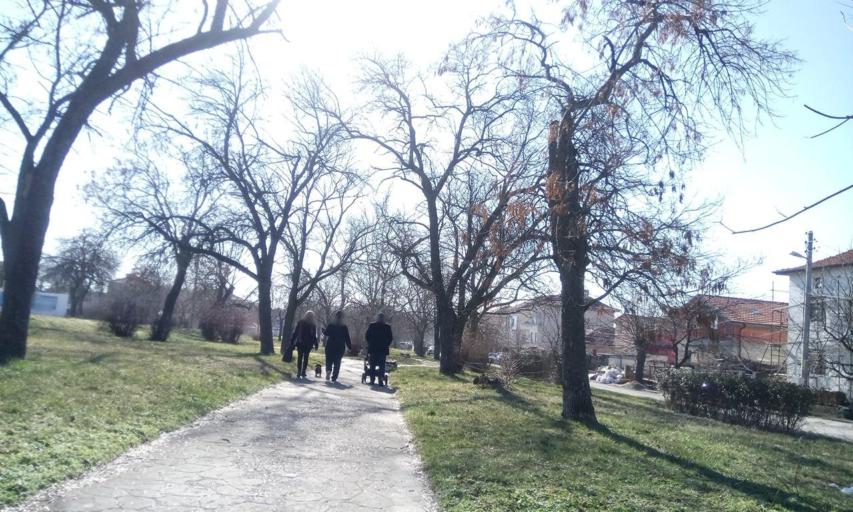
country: BG
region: Plovdiv
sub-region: Obshtina Khisarya
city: Khisarya
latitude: 42.5126
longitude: 24.7162
